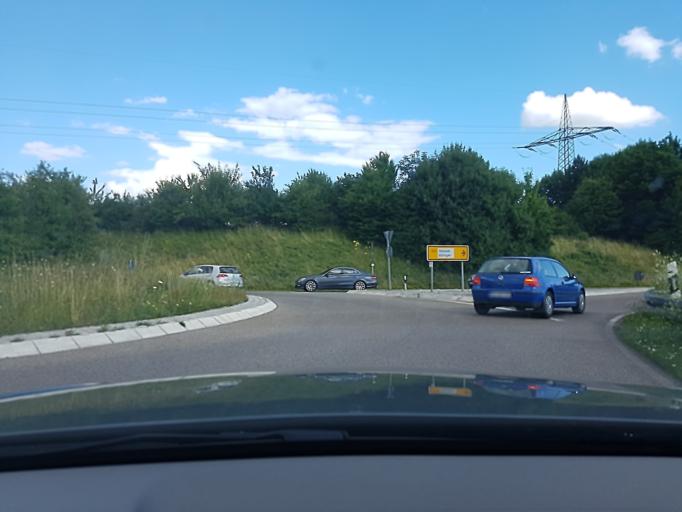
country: DE
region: Baden-Wuerttemberg
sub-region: Tuebingen Region
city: Ulm
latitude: 48.4352
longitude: 10.0117
